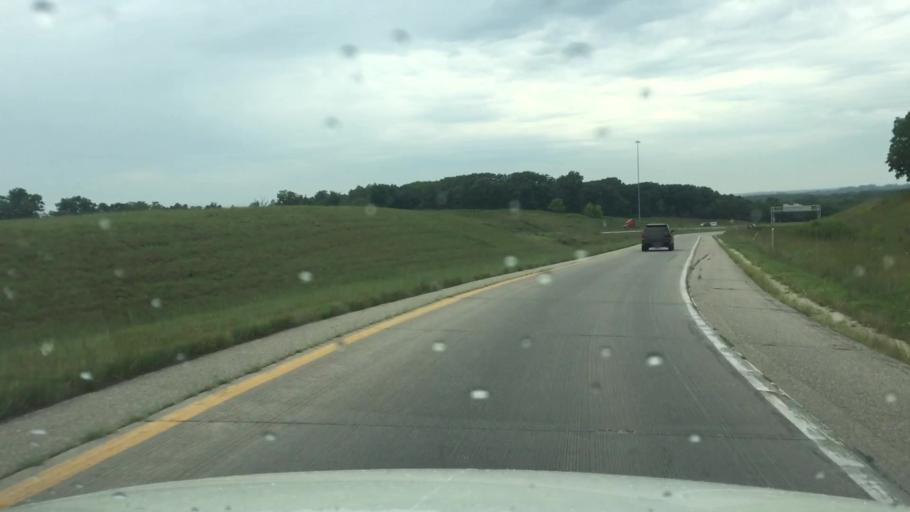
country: US
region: Iowa
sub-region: Warren County
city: Carlisle
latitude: 41.5074
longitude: -93.5752
